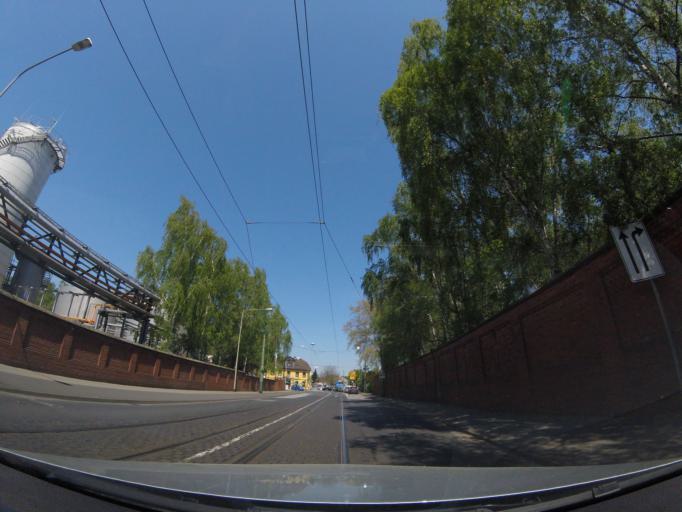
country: DE
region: Hesse
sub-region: Regierungsbezirk Darmstadt
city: Offenbach
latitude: 50.1318
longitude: 8.7674
